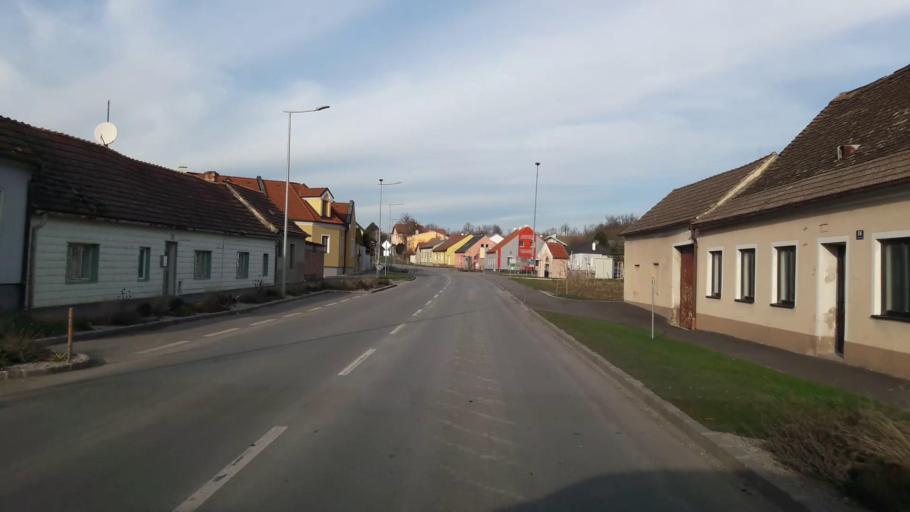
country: AT
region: Lower Austria
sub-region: Politischer Bezirk Mistelbach
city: Gaweinstal
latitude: 48.4804
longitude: 16.5933
